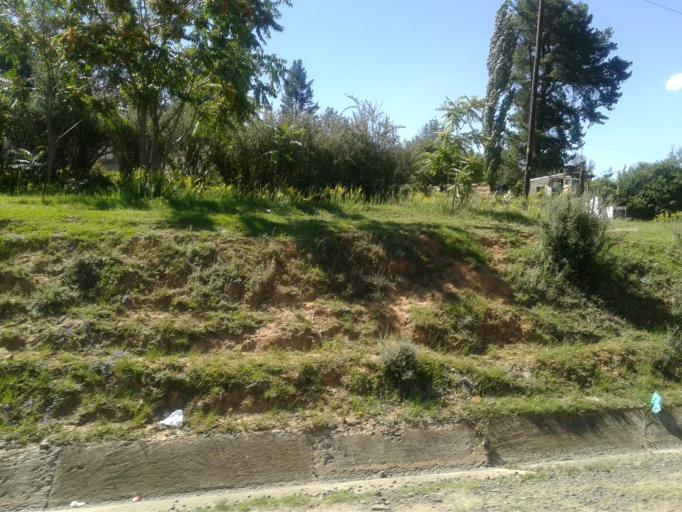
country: LS
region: Butha-Buthe
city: Butha-Buthe
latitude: -28.7565
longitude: 28.2597
